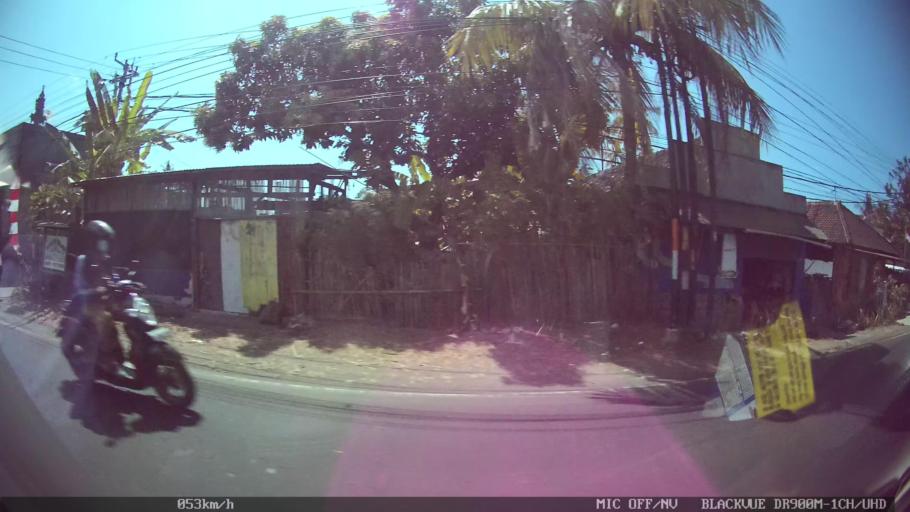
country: ID
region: Bali
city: Banjar Bunutpanggang
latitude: -8.1756
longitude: 115.0039
